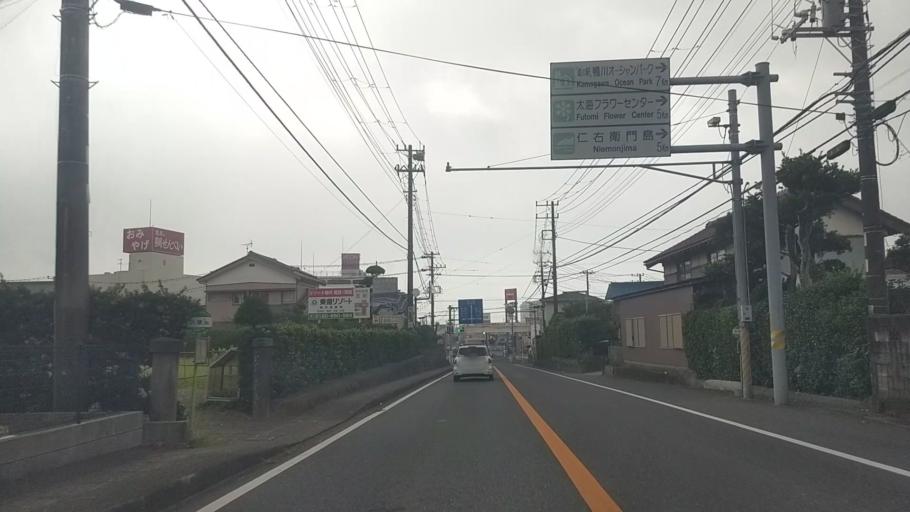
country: JP
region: Chiba
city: Kawaguchi
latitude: 35.1101
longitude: 140.1001
